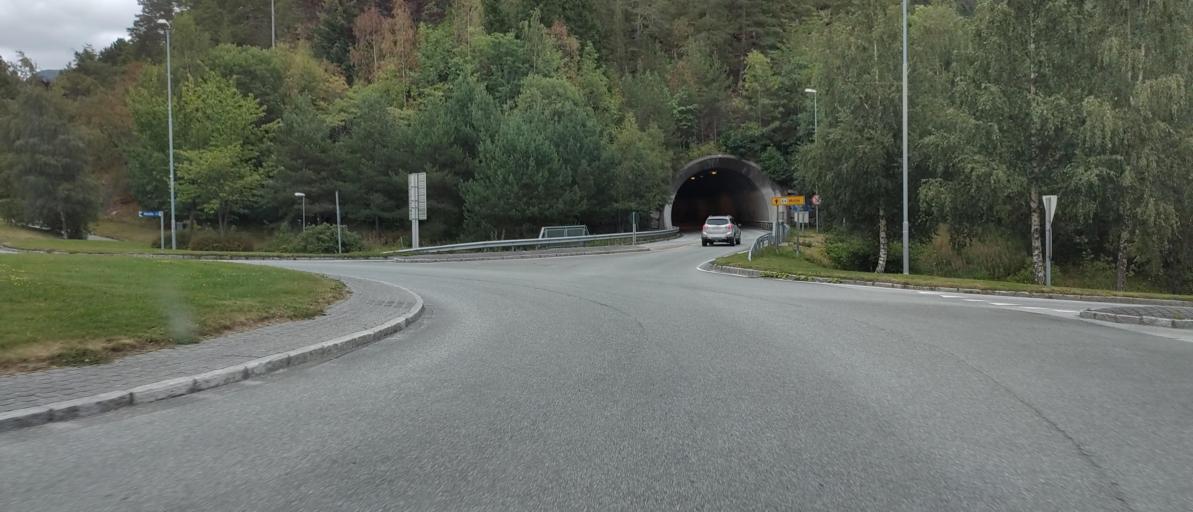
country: NO
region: More og Romsdal
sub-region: Rauma
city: Andalsnes
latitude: 62.5625
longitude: 7.6902
